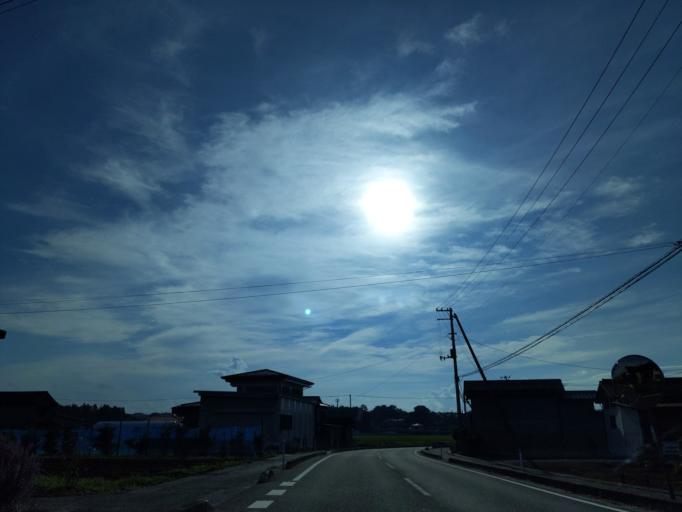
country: JP
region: Fukushima
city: Sukagawa
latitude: 37.2873
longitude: 140.4027
